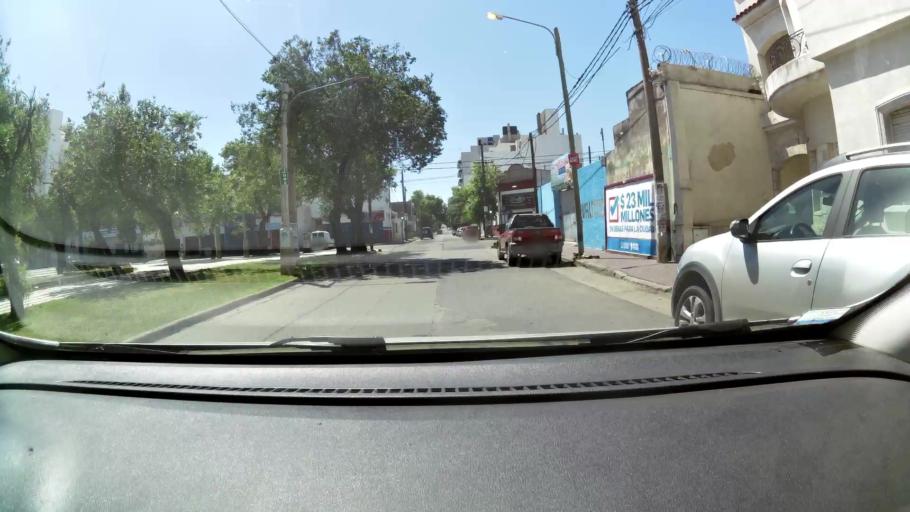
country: AR
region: Cordoba
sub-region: Departamento de Capital
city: Cordoba
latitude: -31.4002
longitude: -64.1956
